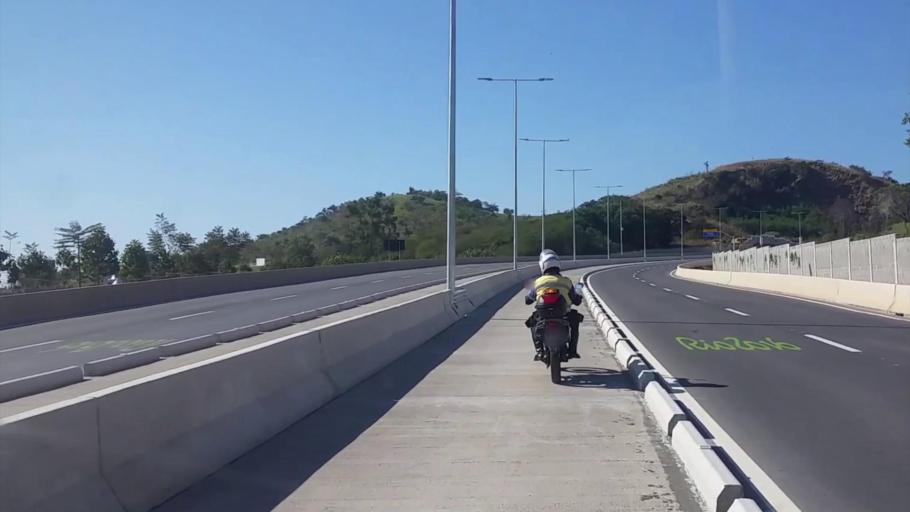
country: BR
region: Rio de Janeiro
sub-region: Nilopolis
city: Nilopolis
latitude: -22.8779
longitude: -43.4028
